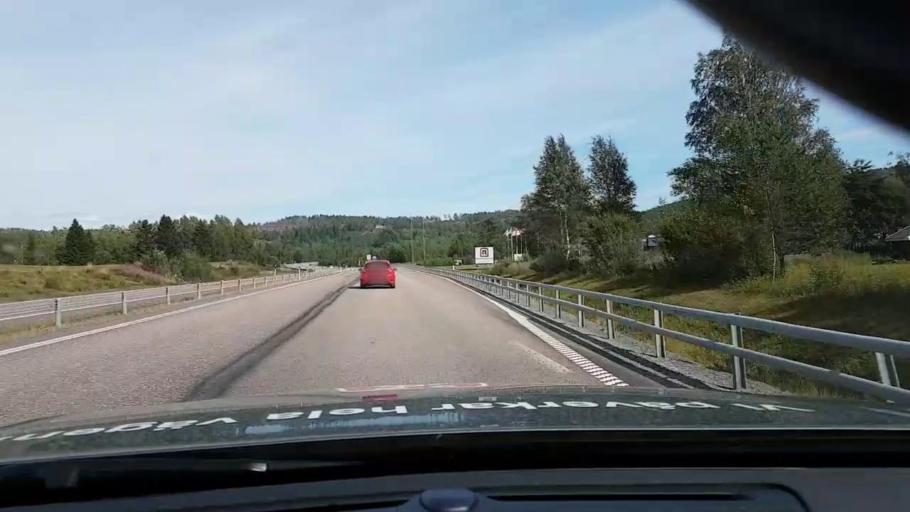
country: SE
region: Vaesternorrland
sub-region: OErnskoeldsviks Kommun
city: Ornskoldsvik
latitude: 63.3107
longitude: 18.7849
